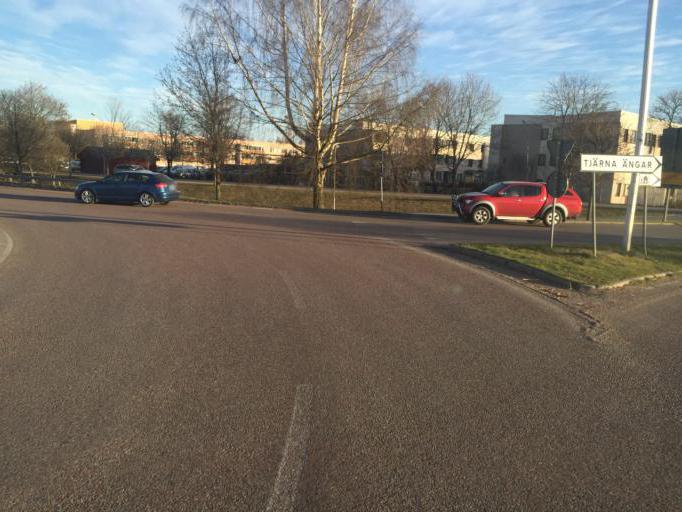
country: SE
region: Dalarna
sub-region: Borlange Kommun
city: Borlaenge
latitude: 60.4954
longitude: 15.4022
